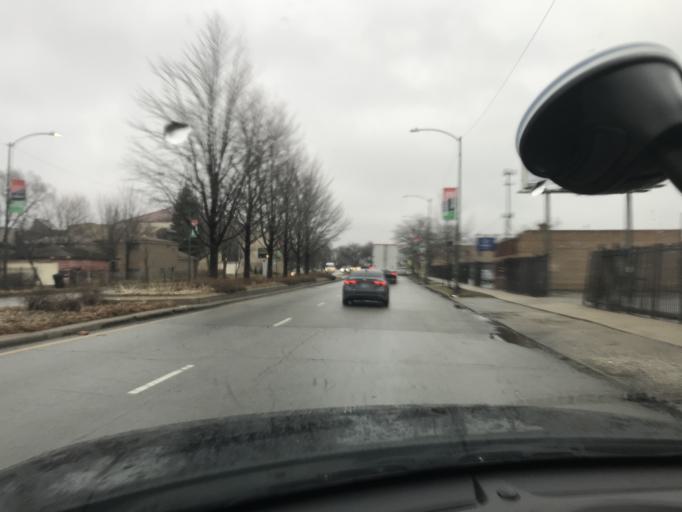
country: US
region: Illinois
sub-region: Cook County
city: Calumet Park
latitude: 41.7215
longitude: -87.6358
